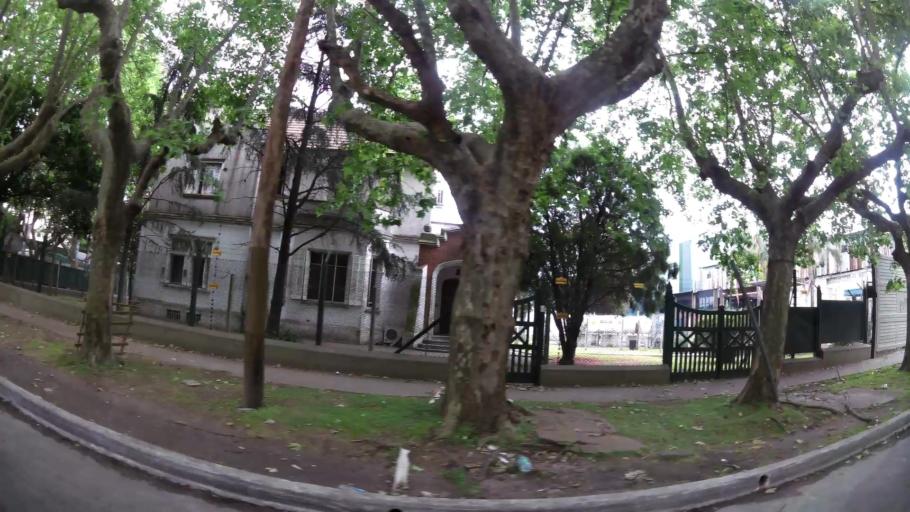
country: AR
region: Buenos Aires
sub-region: Partido de Quilmes
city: Quilmes
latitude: -34.7320
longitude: -58.2584
